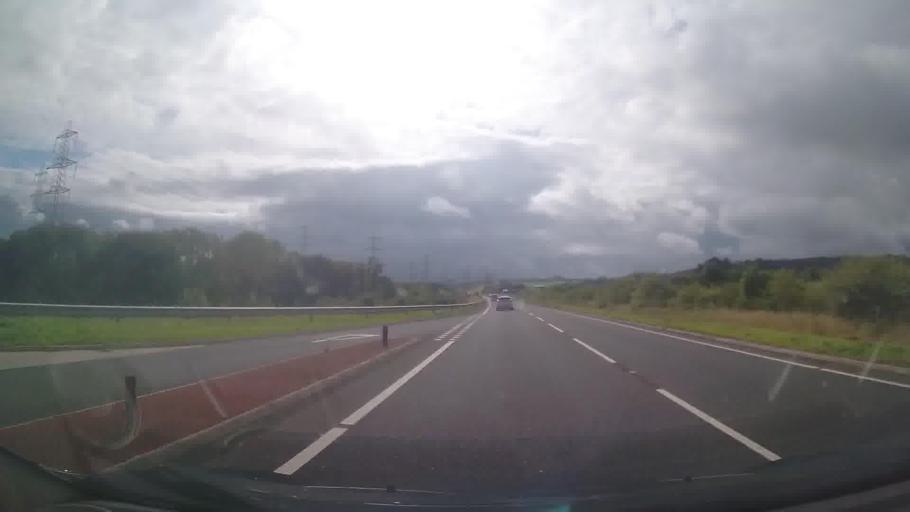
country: GB
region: Wales
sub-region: Carmarthenshire
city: Llanddowror
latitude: 51.7983
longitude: -4.5567
